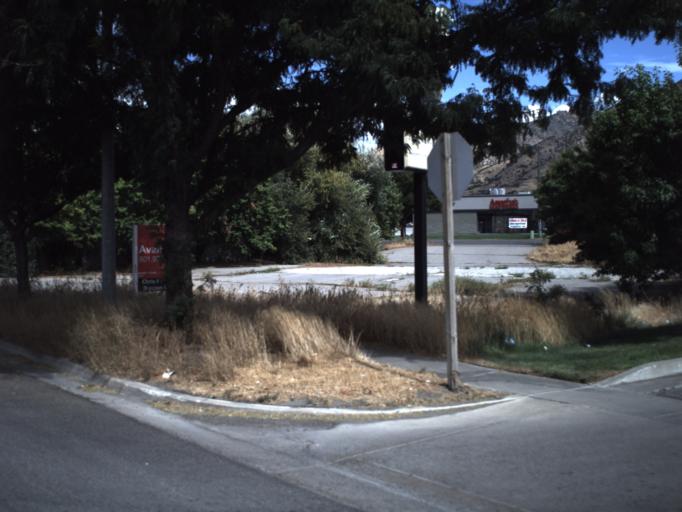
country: US
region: Utah
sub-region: Cache County
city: River Heights
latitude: 41.7158
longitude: -111.8360
